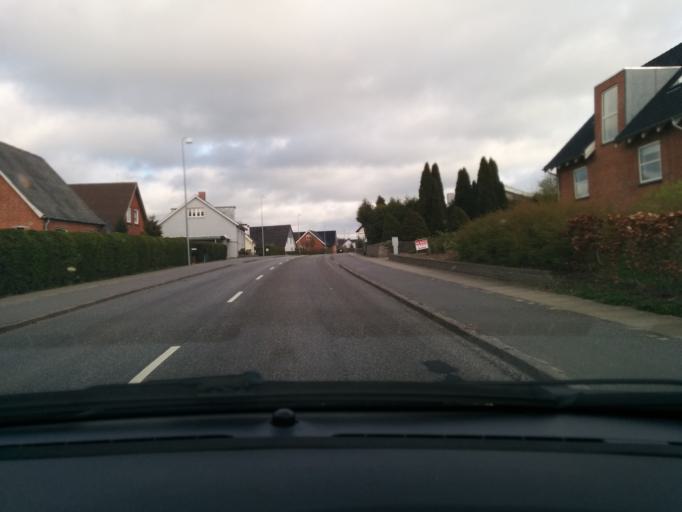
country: DK
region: Central Jutland
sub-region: Favrskov Kommune
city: Hadsten
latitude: 56.3224
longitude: 10.0311
